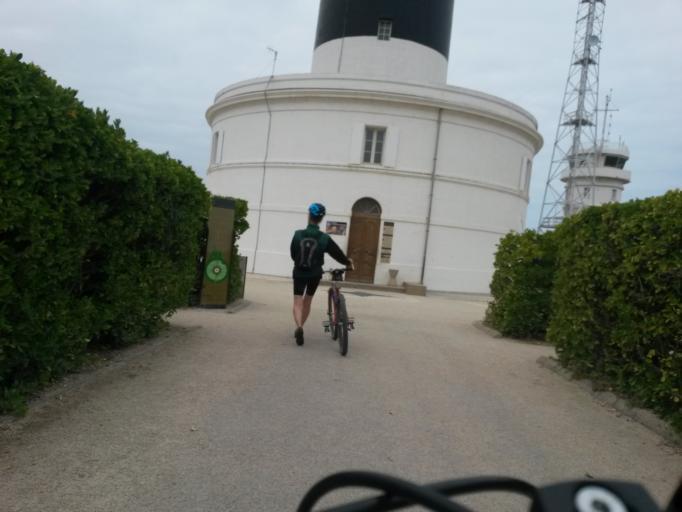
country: FR
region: Poitou-Charentes
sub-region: Departement de la Charente-Maritime
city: Saint-Denis-d'Oleron
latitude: 46.0466
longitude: -1.4099
